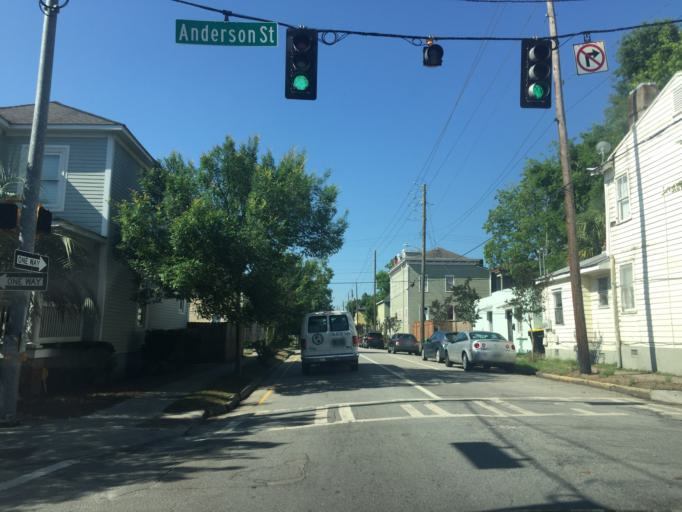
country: US
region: Georgia
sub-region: Chatham County
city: Savannah
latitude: 32.0611
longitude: -81.0928
